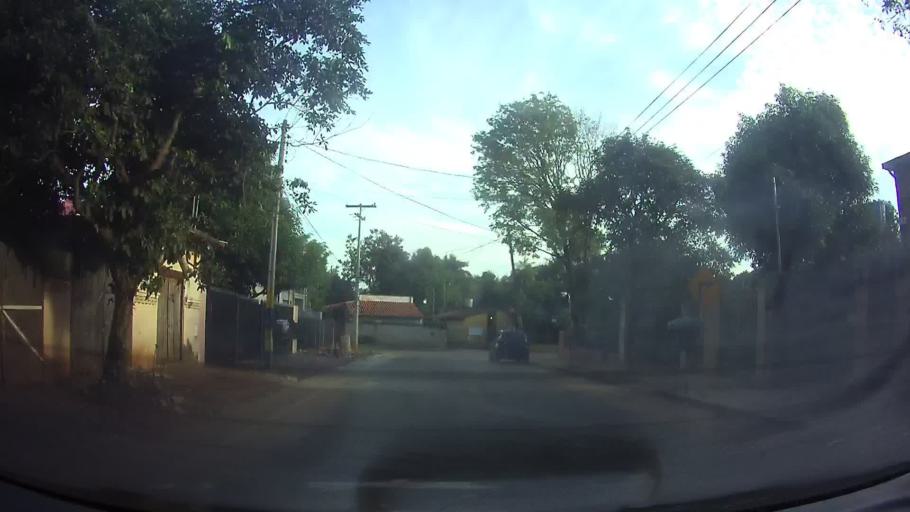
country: PY
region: Central
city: San Lorenzo
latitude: -25.2776
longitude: -57.4826
